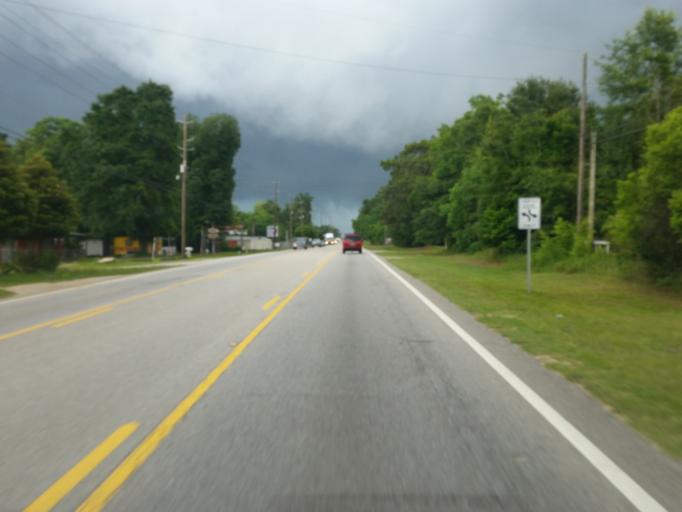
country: US
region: Mississippi
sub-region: Jackson County
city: Hurley
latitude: 30.7931
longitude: -88.3078
